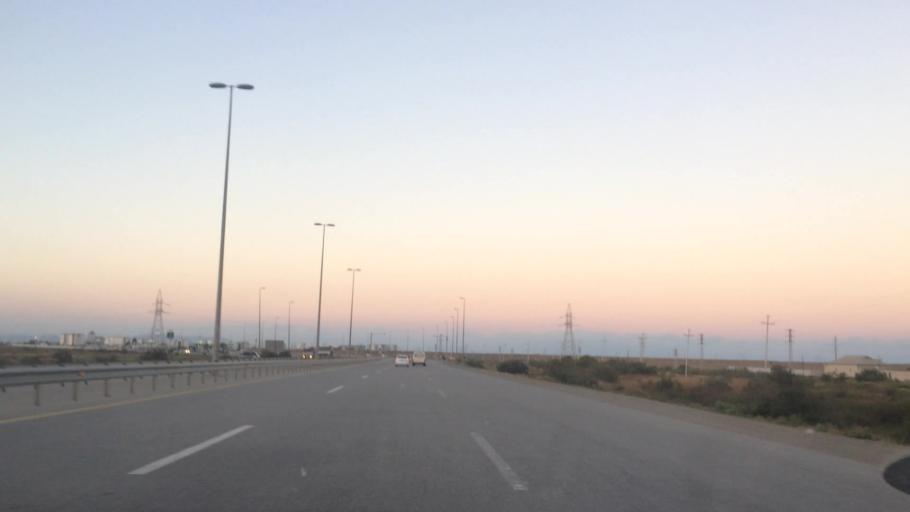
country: AZ
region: Baki
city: Qobustan
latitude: 39.9888
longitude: 49.4296
